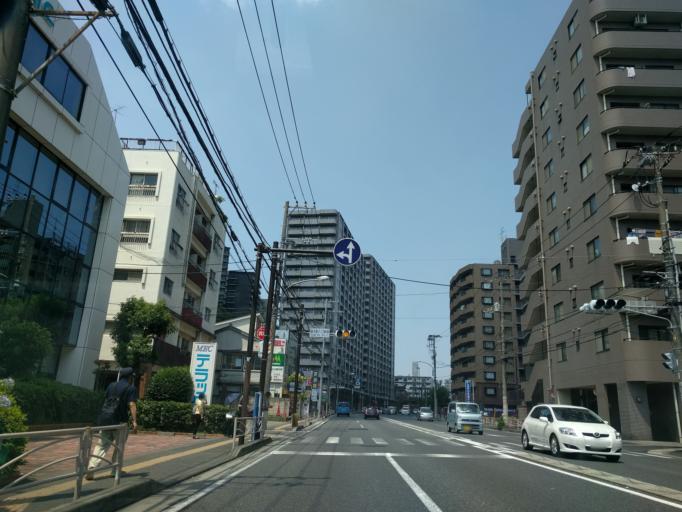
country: JP
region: Kanagawa
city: Yokohama
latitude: 35.4001
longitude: 139.6159
